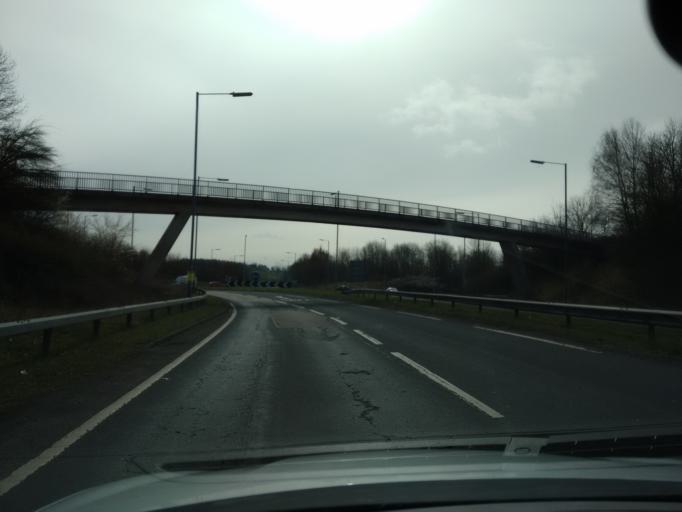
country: GB
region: England
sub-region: Warwickshire
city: Alcester
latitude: 52.2099
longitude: -1.8803
